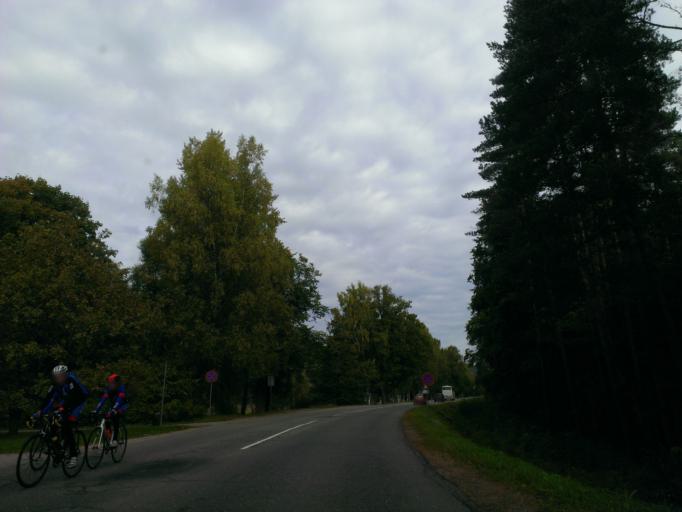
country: LV
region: Sigulda
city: Sigulda
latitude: 57.1706
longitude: 24.8383
